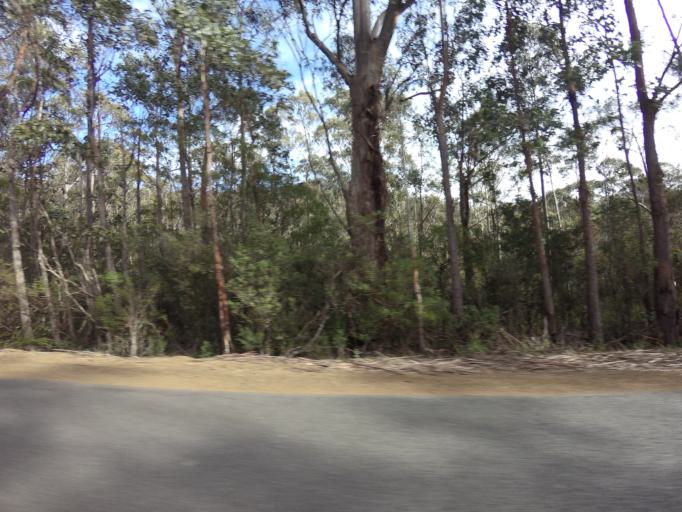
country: AU
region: Tasmania
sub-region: Kingborough
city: Margate
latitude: -43.0048
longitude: 147.1705
